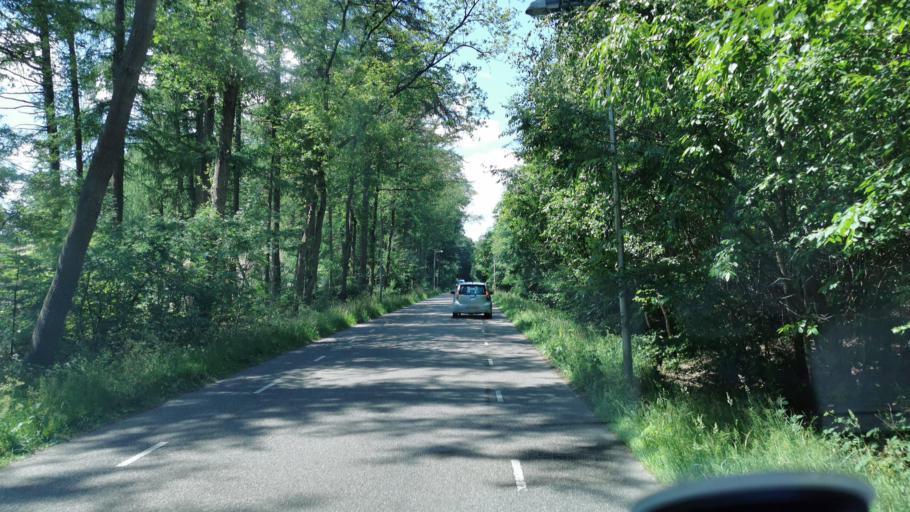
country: NL
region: Overijssel
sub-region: Gemeente Enschede
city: Enschede
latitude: 52.2418
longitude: 6.8640
